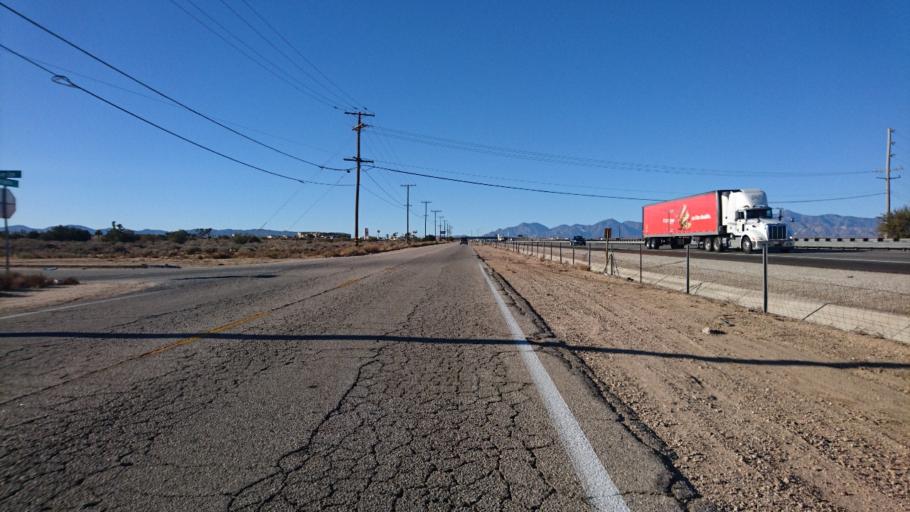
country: US
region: California
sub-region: San Bernardino County
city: Oak Hills
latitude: 34.4345
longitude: -117.3739
